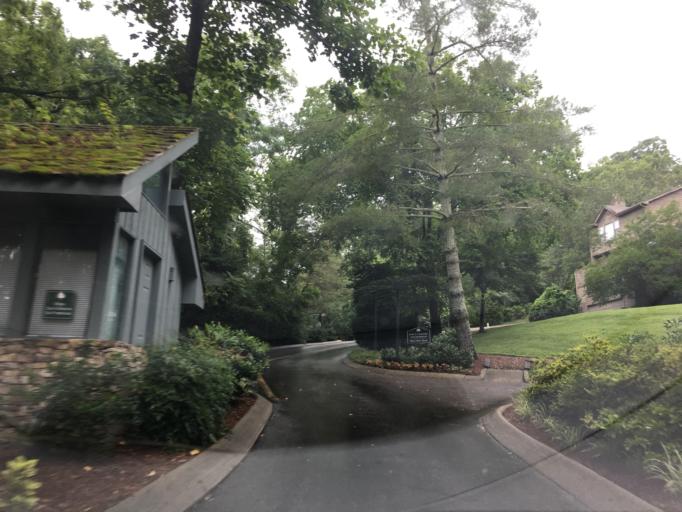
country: US
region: Tennessee
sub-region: Davidson County
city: Belle Meade
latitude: 36.0702
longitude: -86.8979
